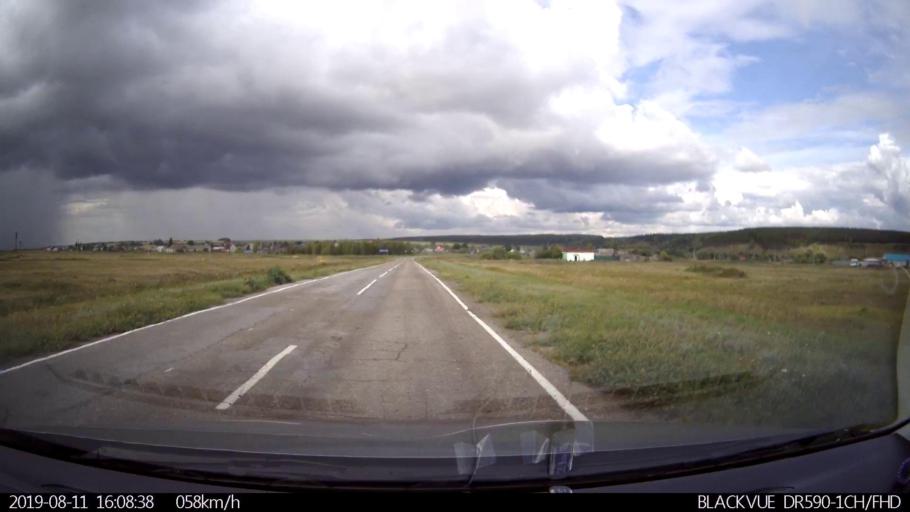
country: RU
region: Ulyanovsk
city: Ignatovka
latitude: 53.9864
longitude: 47.6487
